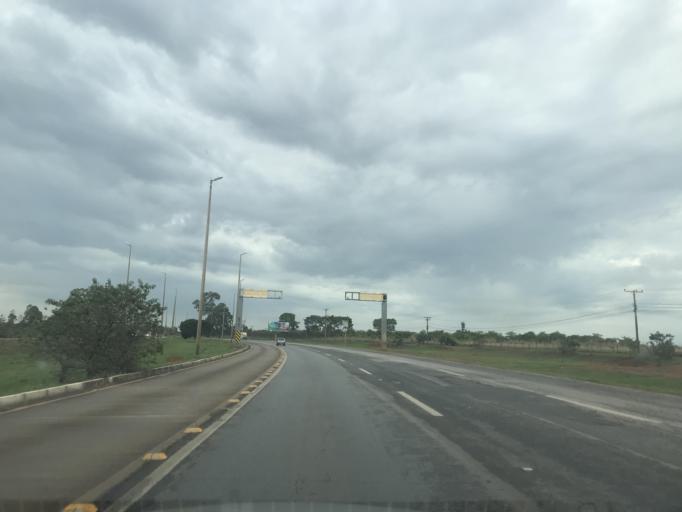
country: BR
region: Federal District
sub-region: Brasilia
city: Brasilia
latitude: -15.9517
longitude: -47.9945
